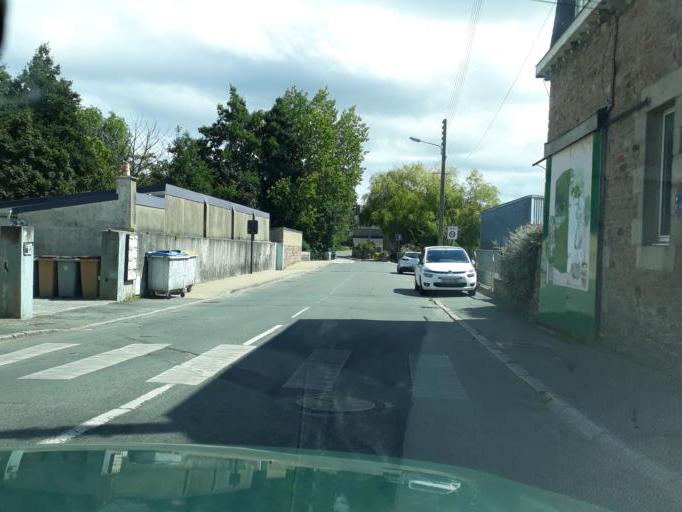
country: FR
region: Brittany
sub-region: Departement des Cotes-d'Armor
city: Paimpol
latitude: 48.7751
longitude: -3.0487
